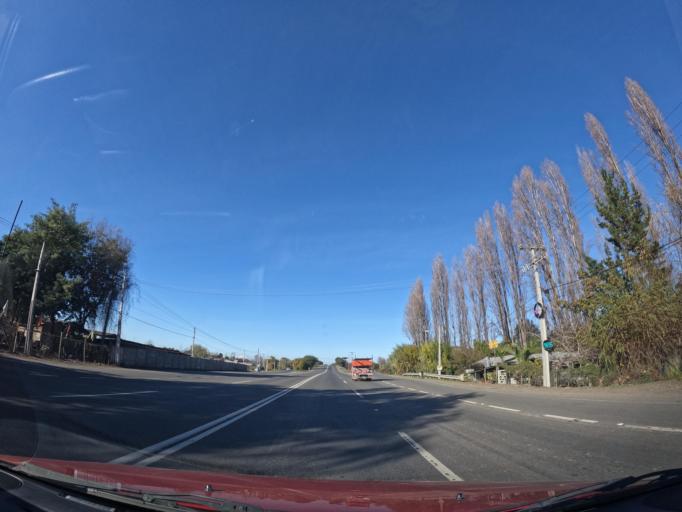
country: CL
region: Maule
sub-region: Provincia de Linares
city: San Javier
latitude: -35.6246
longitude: -71.7528
